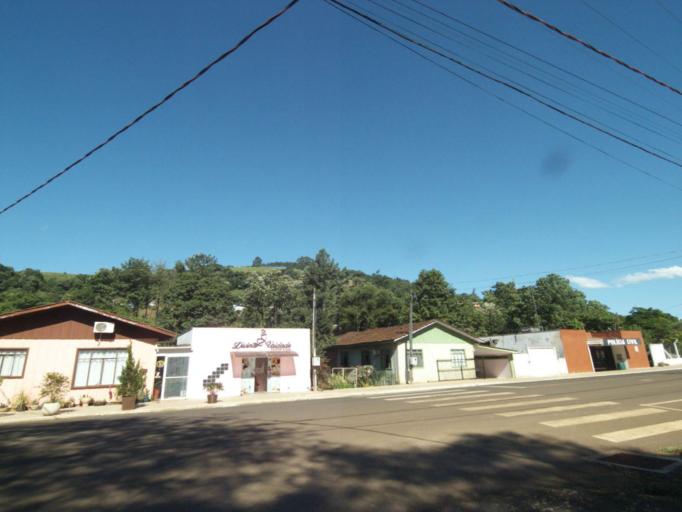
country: BR
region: Parana
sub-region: Ampere
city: Ampere
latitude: -26.1688
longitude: -53.3636
